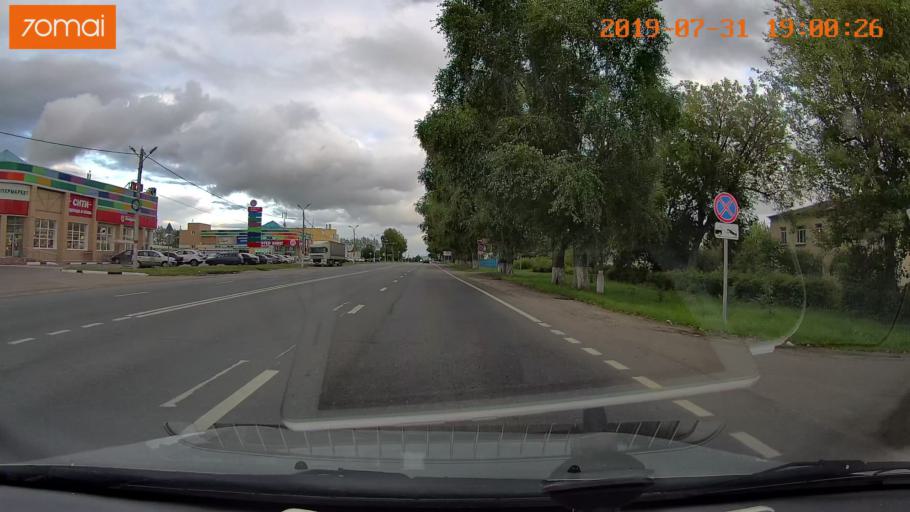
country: RU
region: Moskovskaya
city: Raduzhnyy
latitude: 55.1332
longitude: 38.7241
